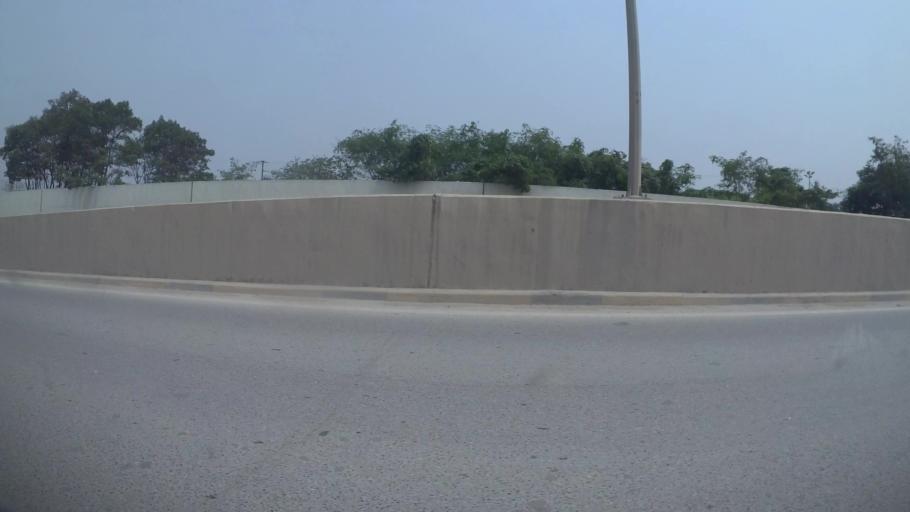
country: VN
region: Ha Noi
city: Cau Dien
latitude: 21.0095
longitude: 105.7425
